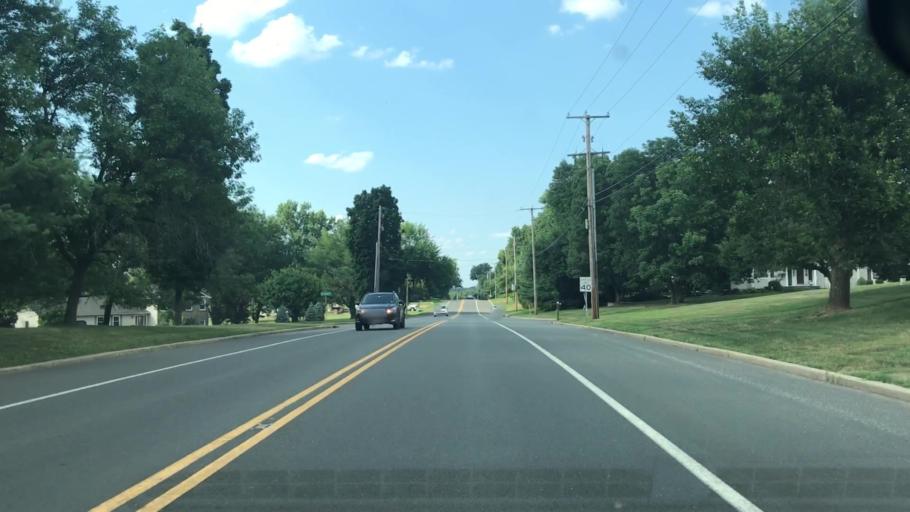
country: US
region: New Jersey
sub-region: Hunterdon County
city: Flemington
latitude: 40.5062
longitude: -74.8083
